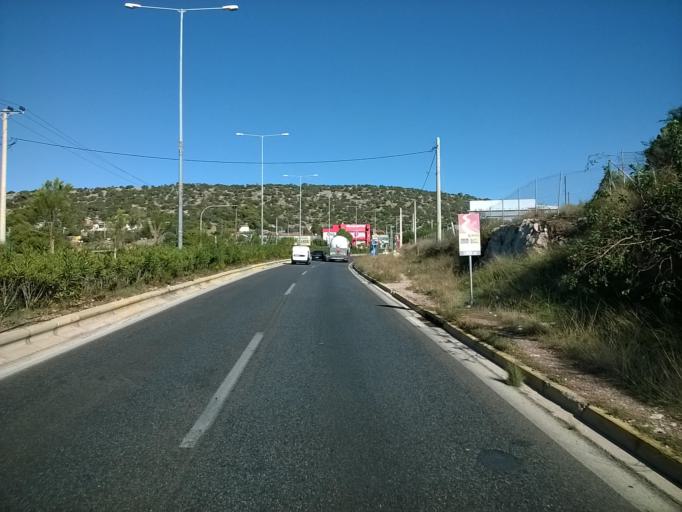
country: GR
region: Attica
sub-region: Nomarchia Anatolikis Attikis
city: Kitsi
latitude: 37.8541
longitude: 23.8311
